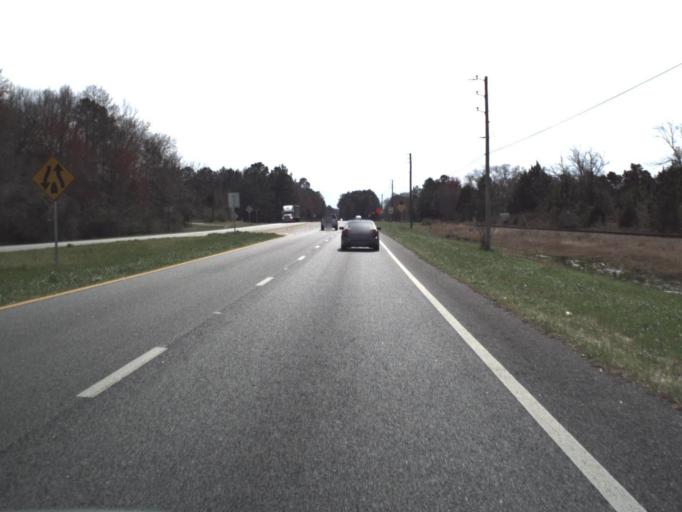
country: US
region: Florida
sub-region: Washington County
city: Chipley
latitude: 30.7076
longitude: -85.3913
